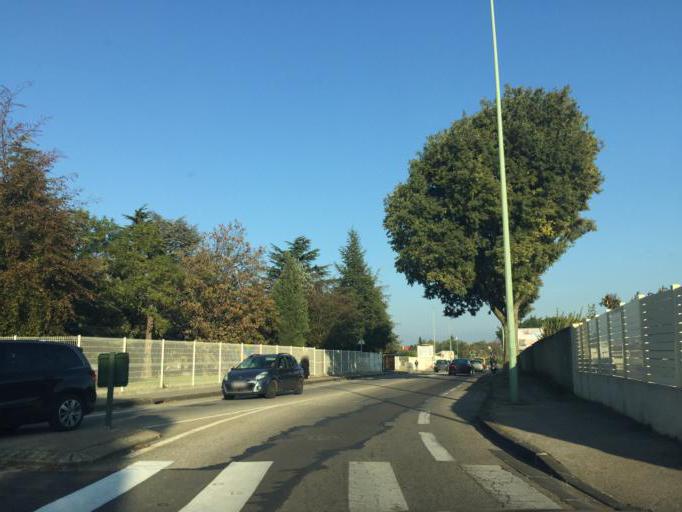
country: FR
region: Rhone-Alpes
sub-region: Departement de la Drome
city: Valence
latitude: 44.9117
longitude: 4.9062
